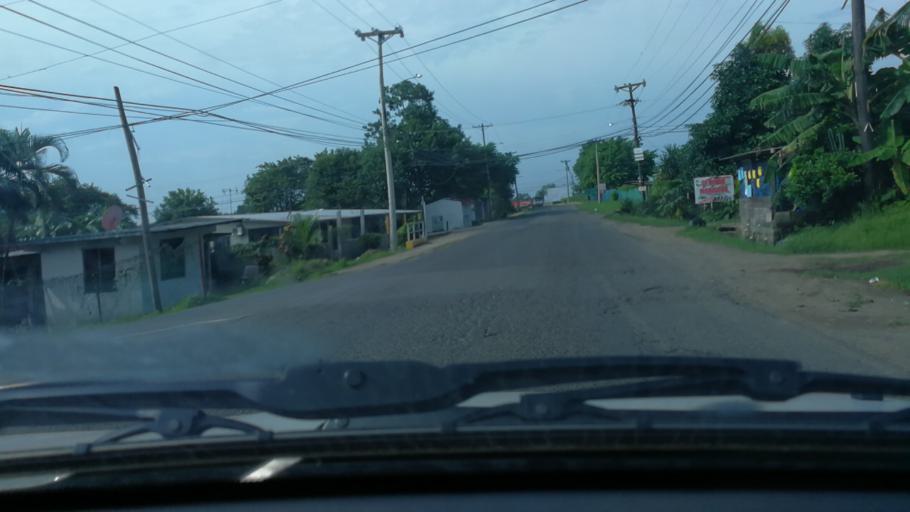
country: PA
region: Panama
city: Pacora
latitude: 9.0911
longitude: -79.2885
